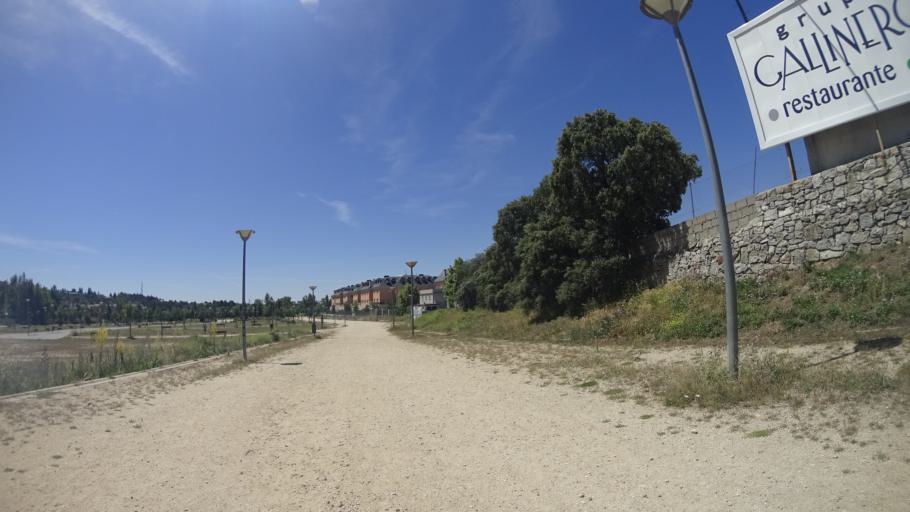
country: ES
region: Madrid
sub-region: Provincia de Madrid
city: Collado-Villalba
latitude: 40.6438
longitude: -4.0069
